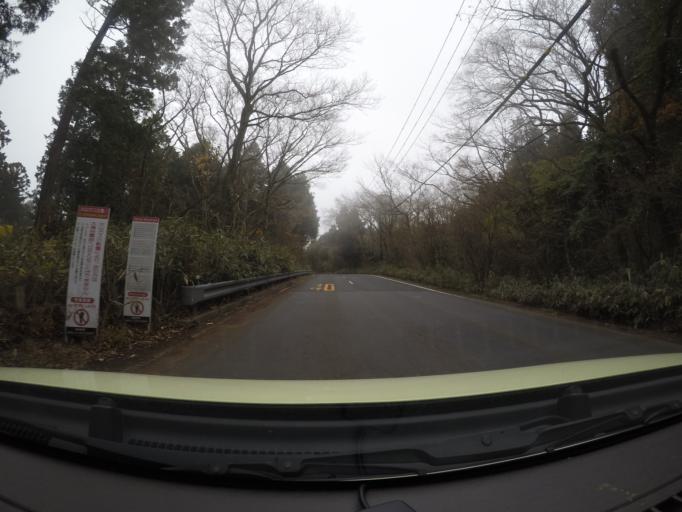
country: JP
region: Kanagawa
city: Hakone
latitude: 35.2485
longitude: 139.0138
